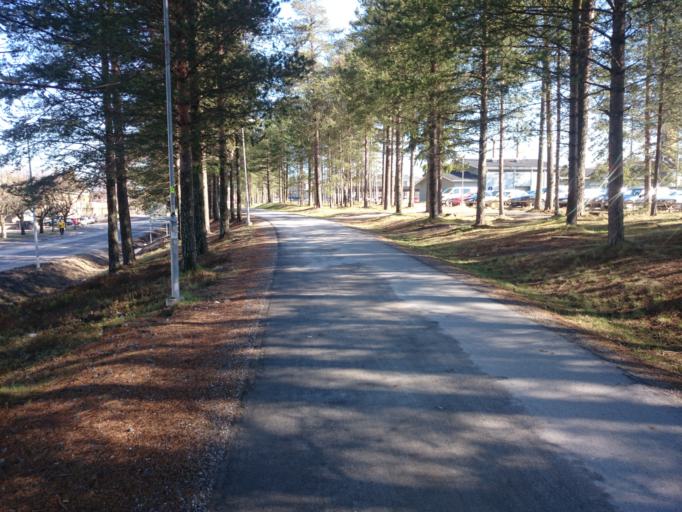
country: SE
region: Vaesterbotten
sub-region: Umea Kommun
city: Umea
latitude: 63.8163
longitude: 20.3043
